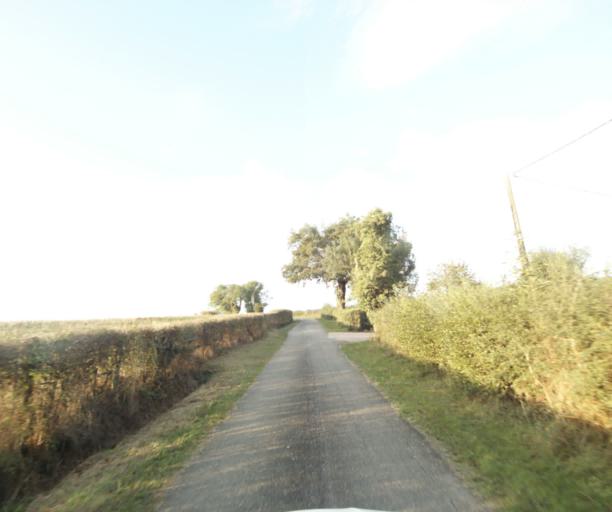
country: FR
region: Bourgogne
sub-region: Departement de Saone-et-Loire
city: Charolles
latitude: 46.4389
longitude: 4.3632
